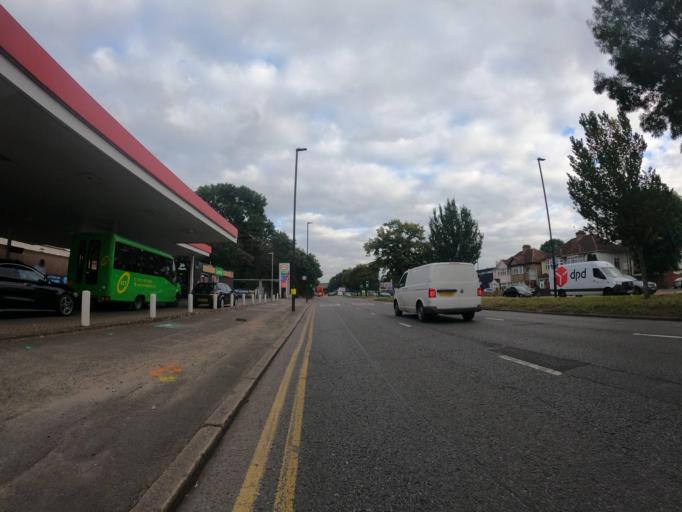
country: GB
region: England
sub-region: Greater London
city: Southall
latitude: 51.5102
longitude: -0.3591
